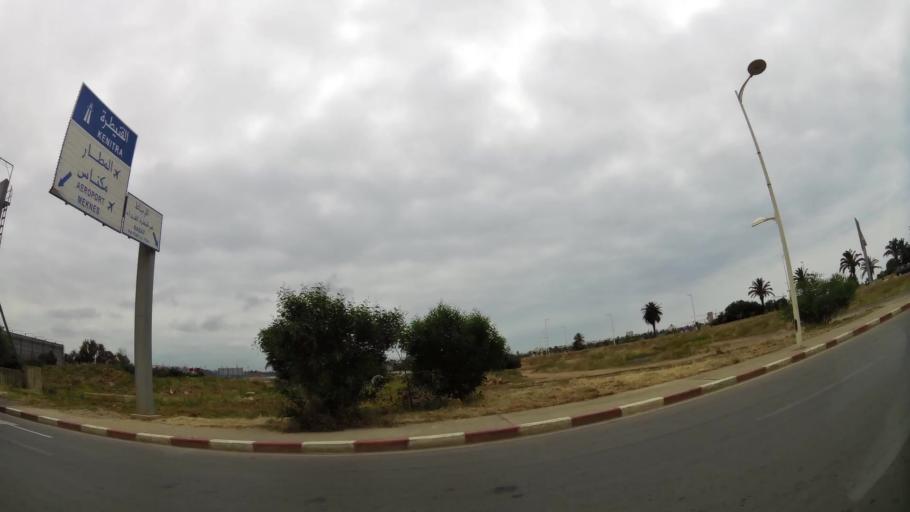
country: MA
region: Rabat-Sale-Zemmour-Zaer
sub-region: Rabat
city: Rabat
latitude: 34.0226
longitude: -6.8037
